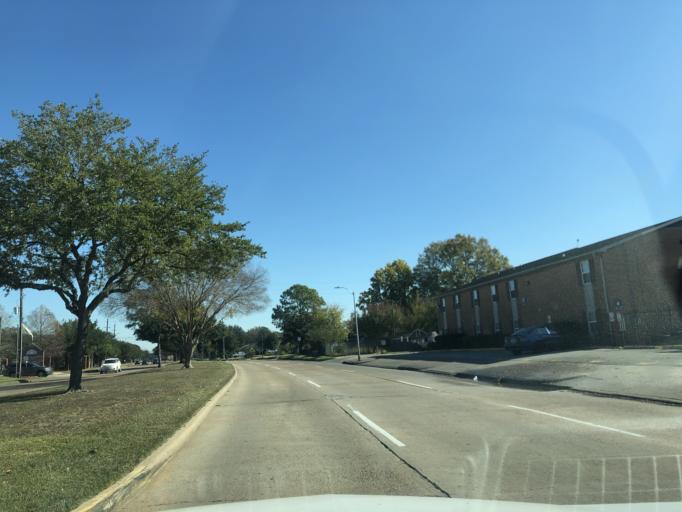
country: US
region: Texas
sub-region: Harris County
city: Bellaire
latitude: 29.6912
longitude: -95.5192
